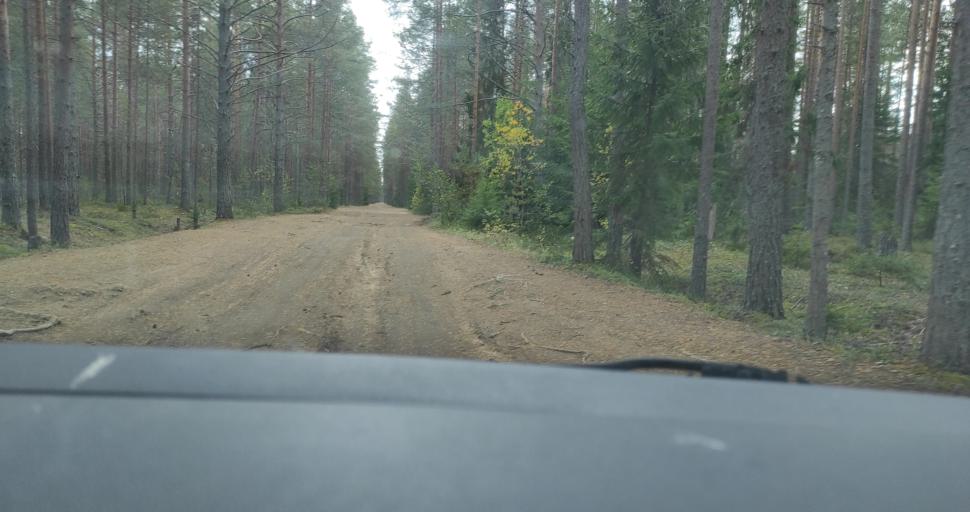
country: RU
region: Leningrad
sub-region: Vsevolzhskij Rajon
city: Vaskelovo
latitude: 60.4127
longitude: 30.3289
